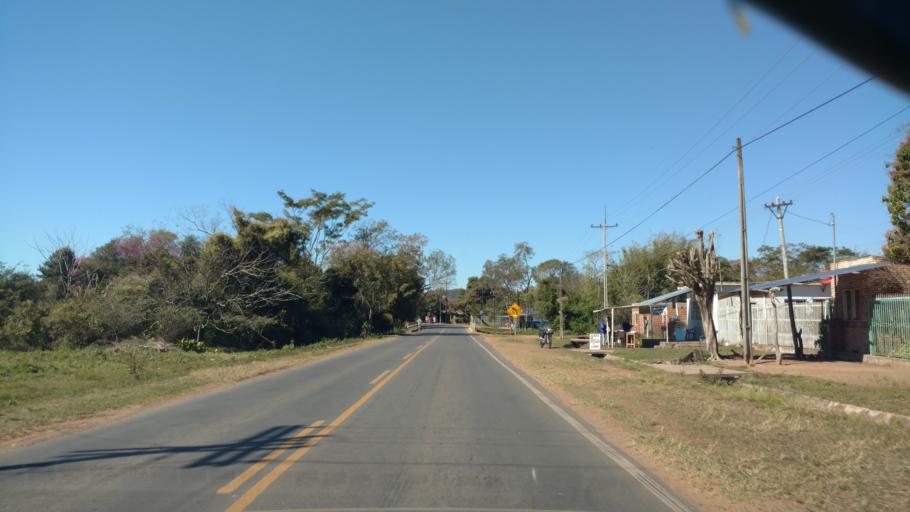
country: PY
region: Paraguari
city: Pirayu
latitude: -25.4568
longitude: -57.2711
